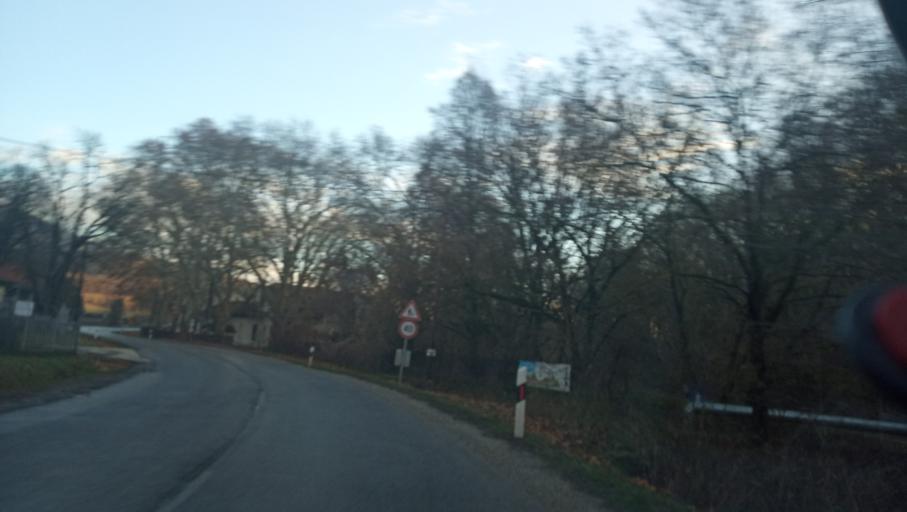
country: HU
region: Pest
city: Csobanka
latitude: 47.6532
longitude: 18.9734
